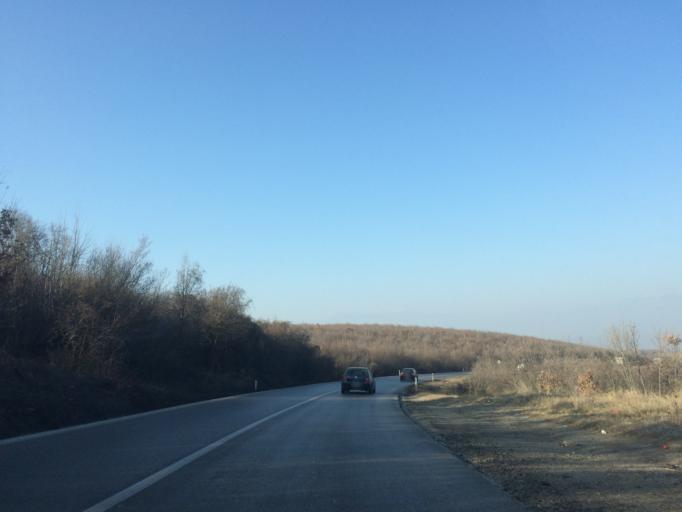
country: XK
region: Pec
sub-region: Komuna e Klines
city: Klina
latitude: 42.5950
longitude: 20.6131
